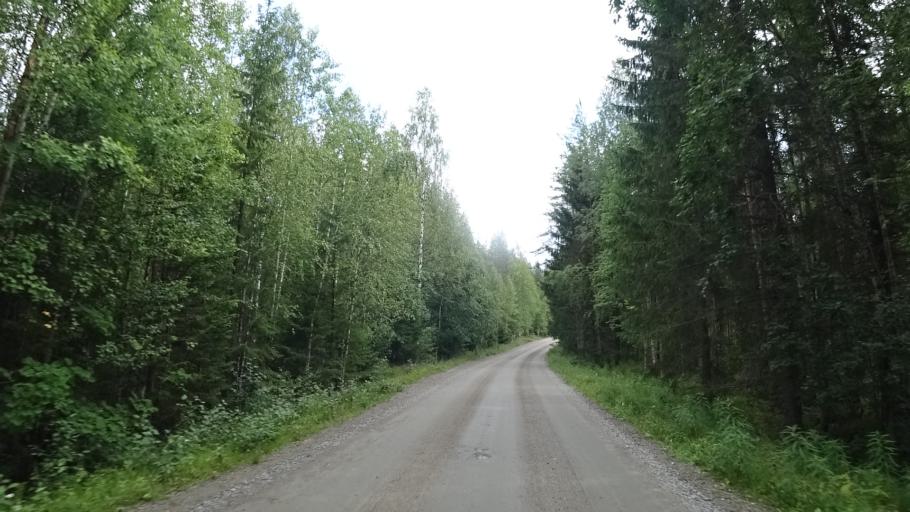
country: FI
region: North Karelia
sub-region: Joensuu
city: Ilomantsi
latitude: 62.9218
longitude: 31.3381
